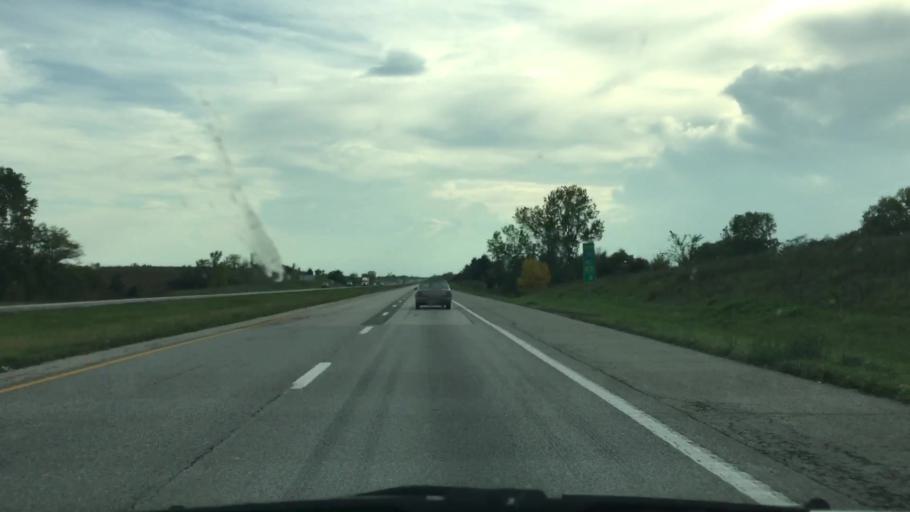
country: US
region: Missouri
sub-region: Harrison County
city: Bethany
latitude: 40.1687
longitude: -94.0234
